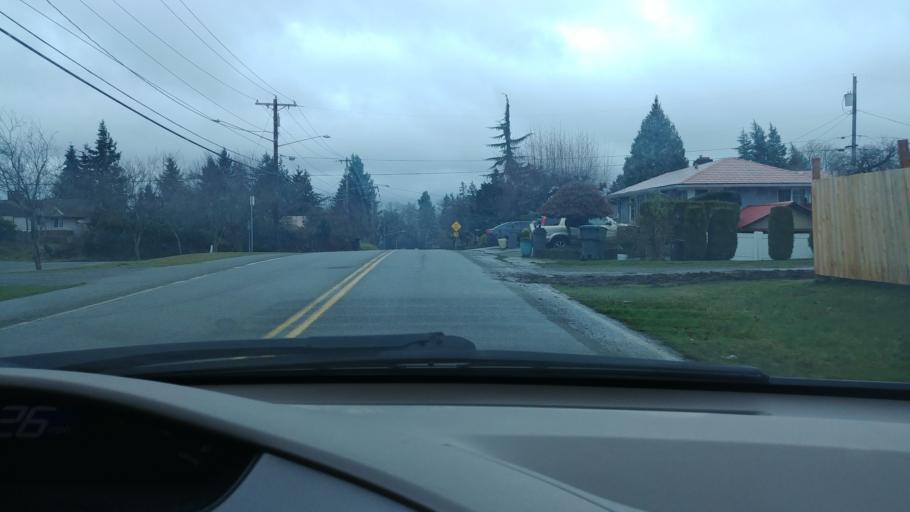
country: US
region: Washington
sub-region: Snohomish County
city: Everett
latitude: 47.9550
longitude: -122.2178
